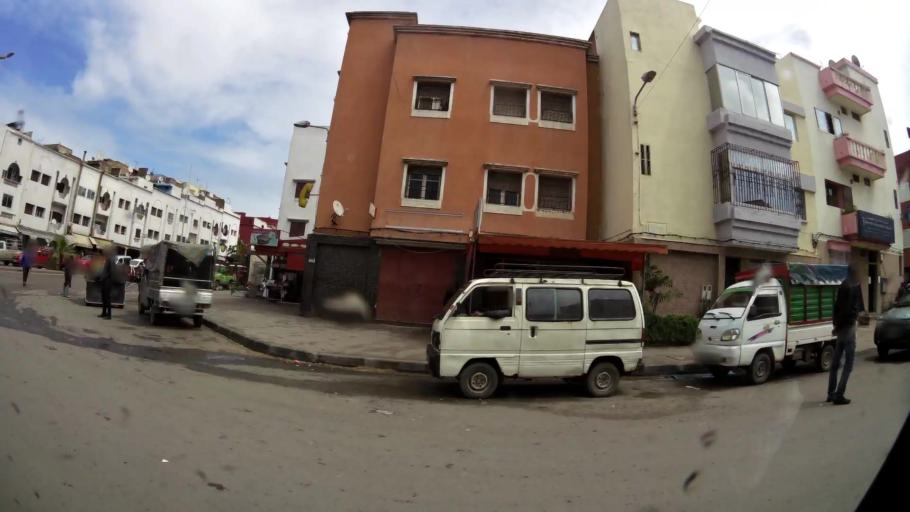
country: MA
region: Grand Casablanca
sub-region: Casablanca
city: Casablanca
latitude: 33.5532
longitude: -7.6890
